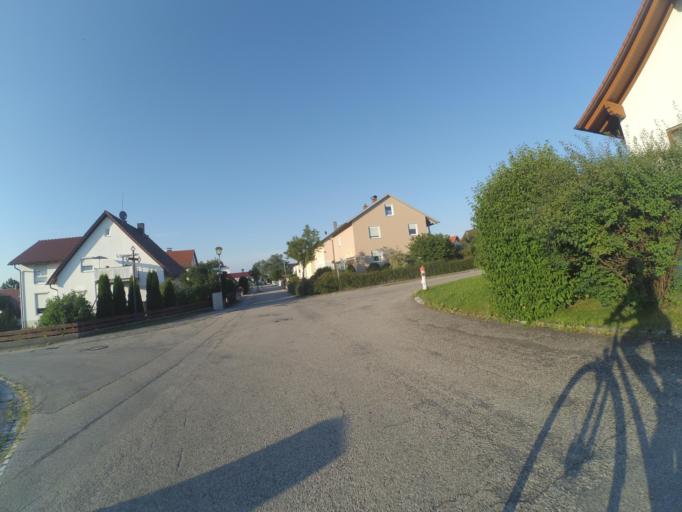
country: DE
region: Bavaria
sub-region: Swabia
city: Bad Worishofen
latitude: 48.0195
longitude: 10.5652
